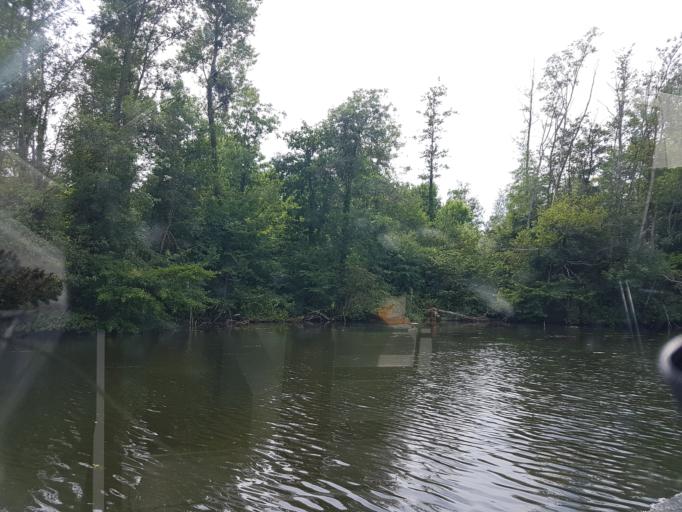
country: FR
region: Bourgogne
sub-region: Departement de l'Yonne
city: Gurgy
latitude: 47.8581
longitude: 3.5560
